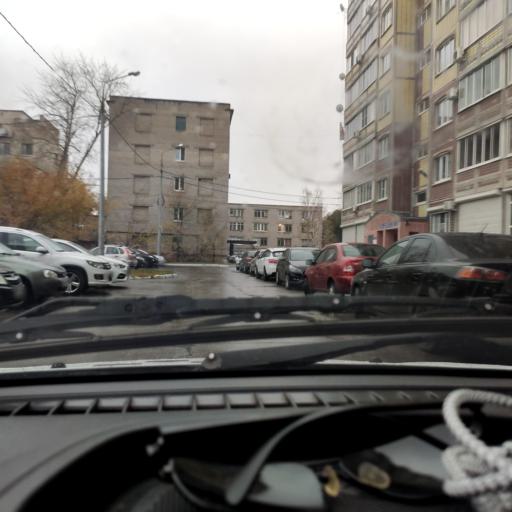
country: RU
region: Samara
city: Zhigulevsk
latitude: 53.4808
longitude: 49.4873
